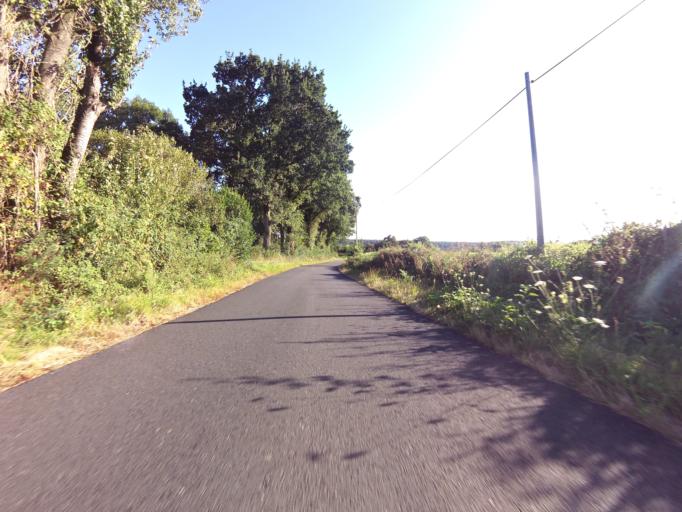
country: FR
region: Brittany
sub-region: Departement du Morbihan
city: Pluherlin
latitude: 47.7203
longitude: -2.3544
